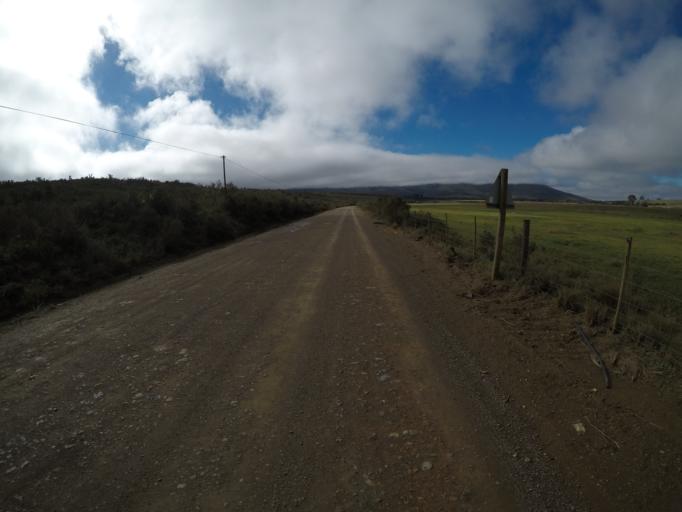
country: ZA
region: Western Cape
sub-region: Cape Winelands District Municipality
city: Ashton
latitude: -34.1250
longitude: 19.8255
